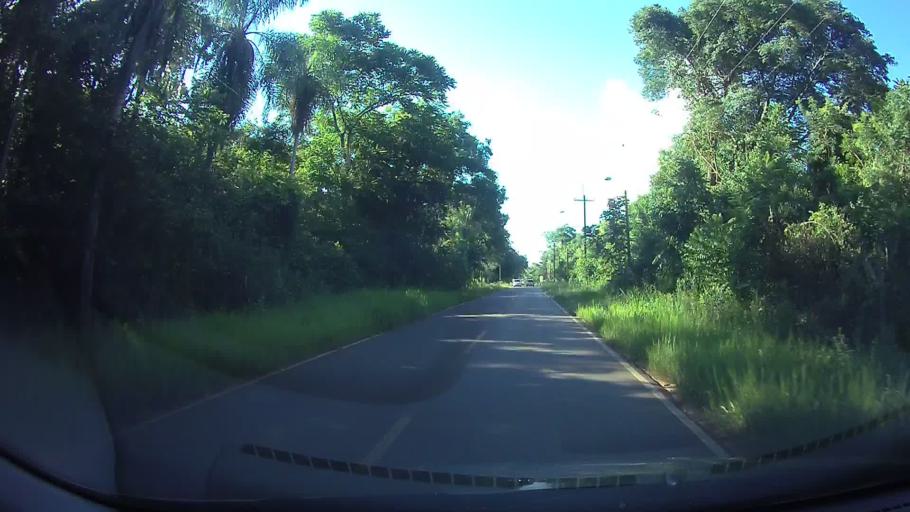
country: PY
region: Central
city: Aregua
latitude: -25.3253
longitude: -57.3889
